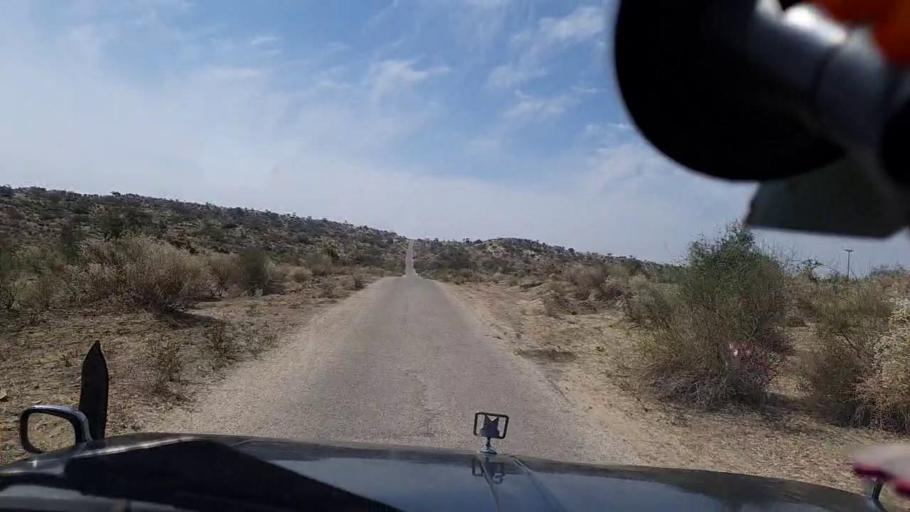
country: PK
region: Sindh
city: Diplo
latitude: 24.3887
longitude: 69.5884
